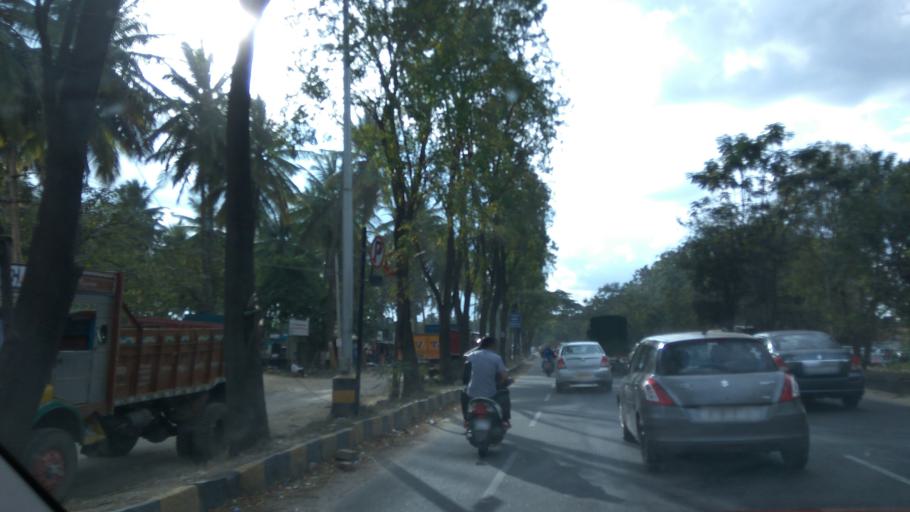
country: IN
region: Karnataka
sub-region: Bangalore Urban
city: Yelahanka
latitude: 13.0432
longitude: 77.6089
